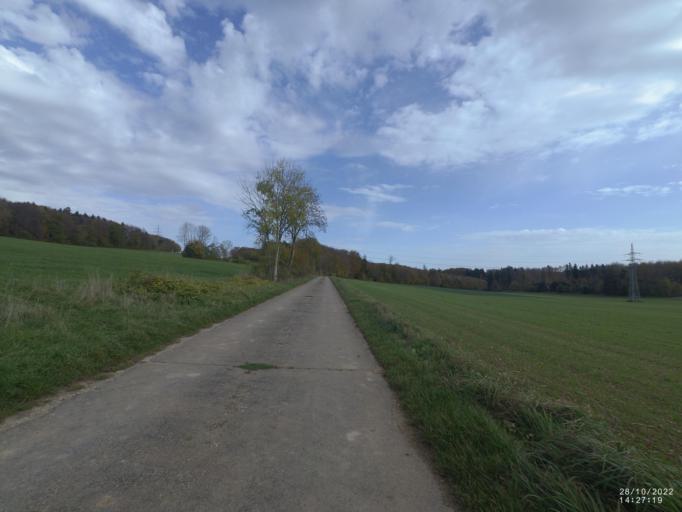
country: DE
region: Baden-Wuerttemberg
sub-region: Tuebingen Region
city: Amstetten
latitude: 48.6039
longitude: 9.8566
